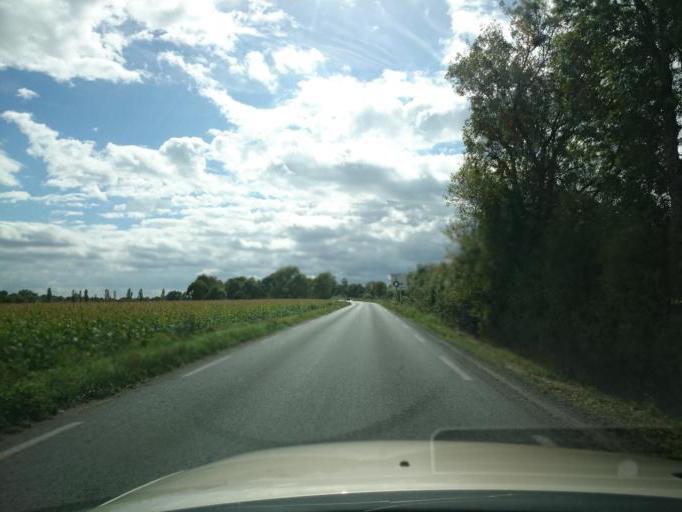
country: FR
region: Aquitaine
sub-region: Departement de la Gironde
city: Saint-Louis-de-Montferrand
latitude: 44.9463
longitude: -0.5583
